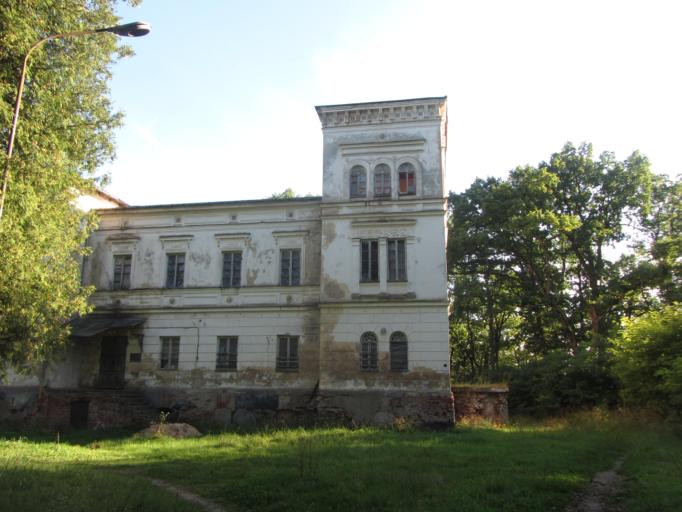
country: LT
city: Vilkija
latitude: 55.0805
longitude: 23.3906
